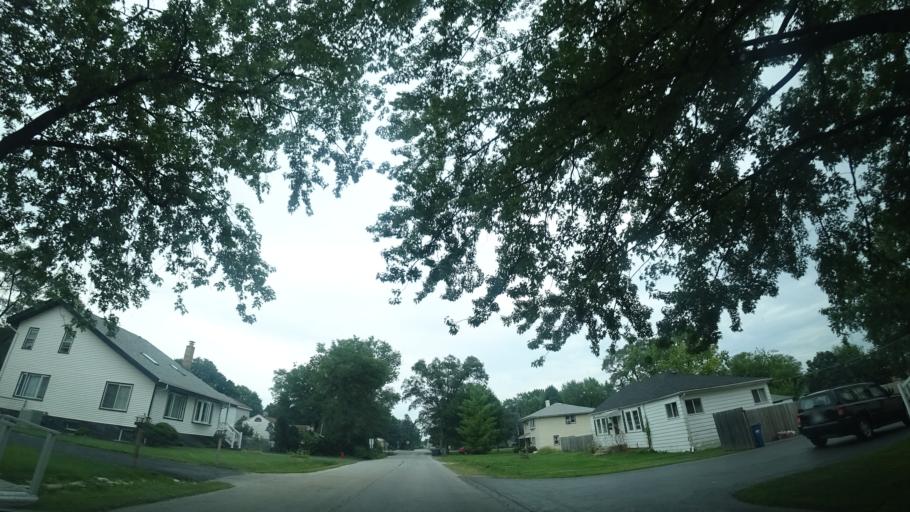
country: US
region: Illinois
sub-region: Cook County
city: Merrionette Park
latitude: 41.6776
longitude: -87.7174
